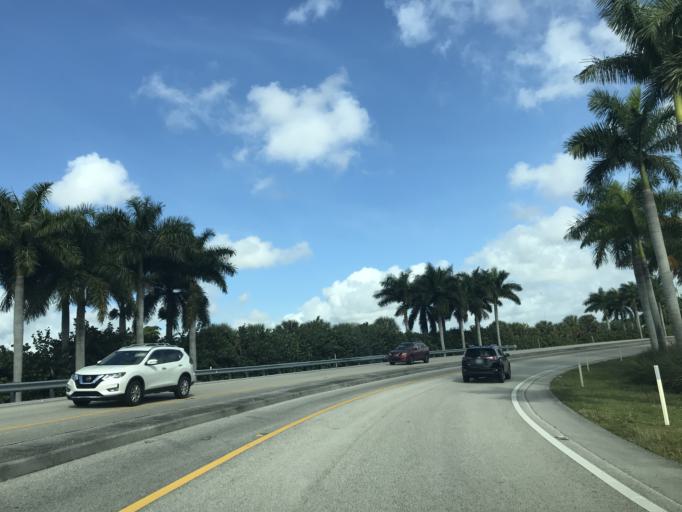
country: US
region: Florida
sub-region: Palm Beach County
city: Boca Del Mar
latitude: 26.3752
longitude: -80.1726
